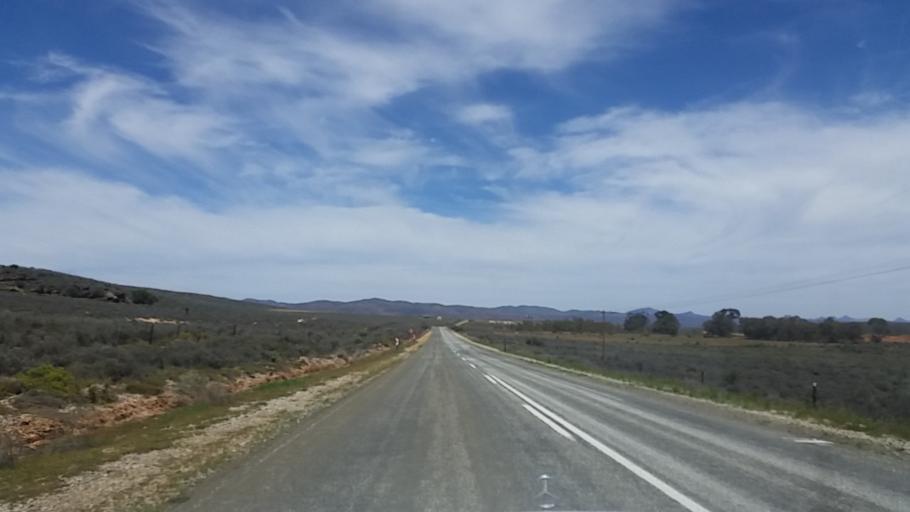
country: ZA
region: Western Cape
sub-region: Eden District Municipality
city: Knysna
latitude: -33.5955
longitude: 23.1512
